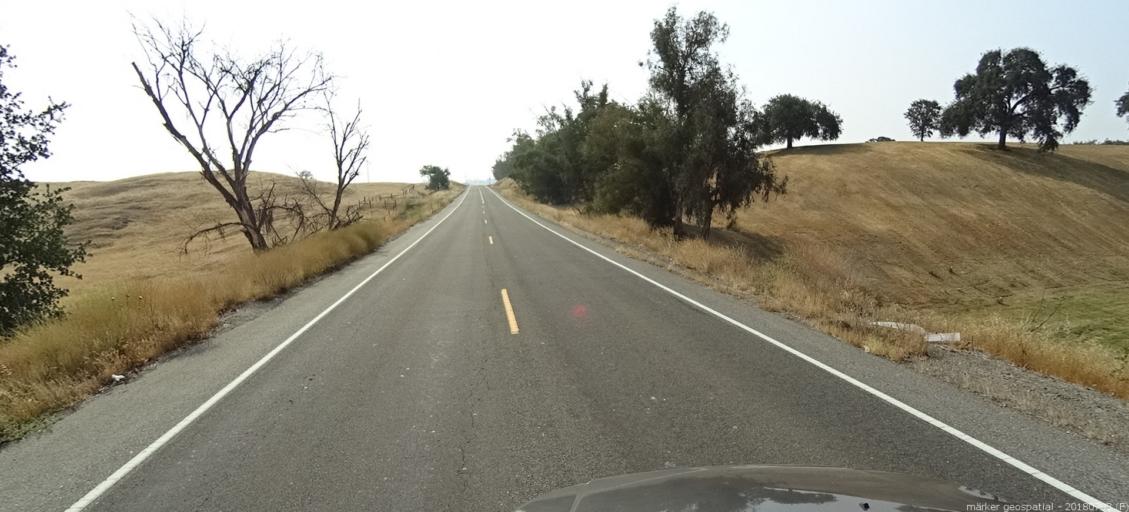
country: US
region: California
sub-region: Madera County
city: Bonadelle Ranchos-Madera Ranchos
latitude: 36.9980
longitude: -119.7251
